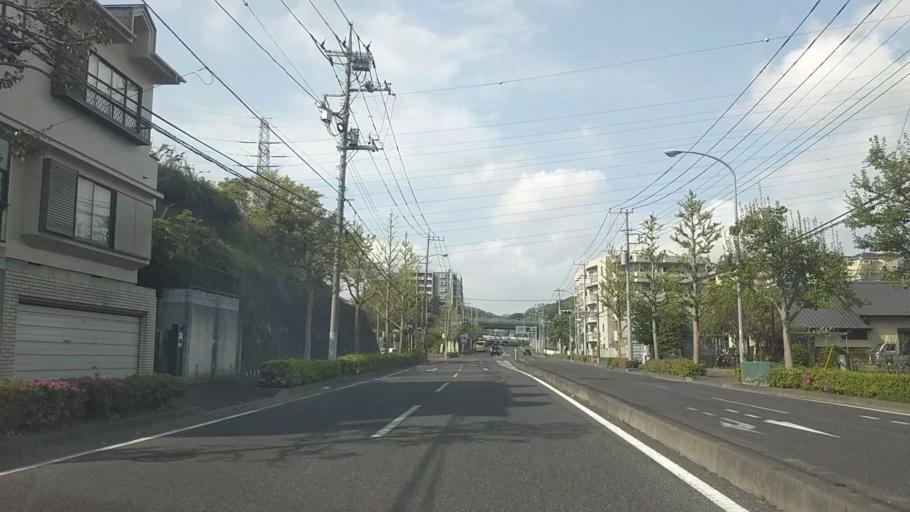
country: JP
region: Kanagawa
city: Kamakura
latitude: 35.3758
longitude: 139.5519
